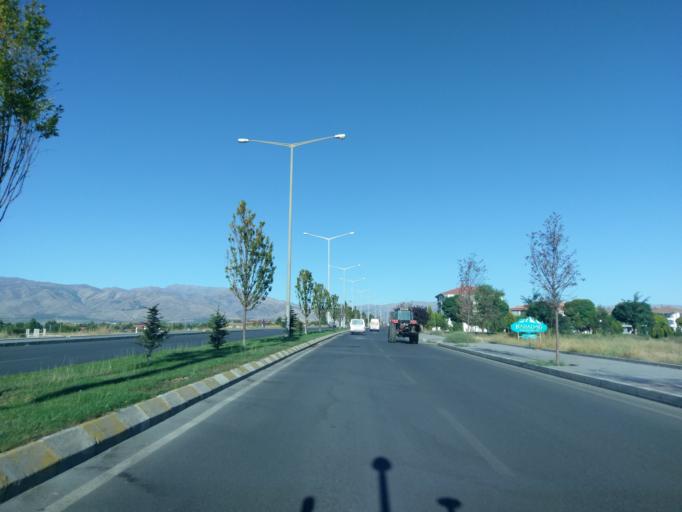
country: TR
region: Erzincan
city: Erzincan
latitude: 39.7488
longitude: 39.4637
